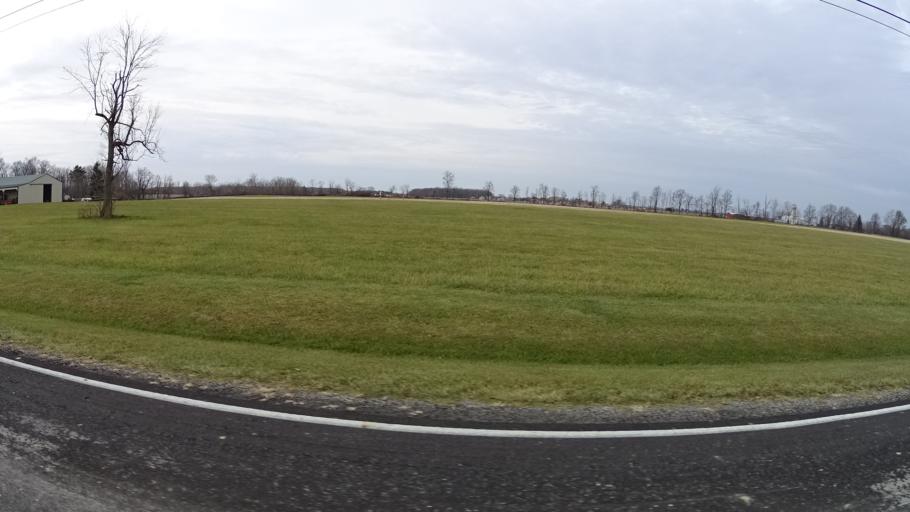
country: US
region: Ohio
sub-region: Lorain County
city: Wellington
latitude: 41.1439
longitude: -82.1697
